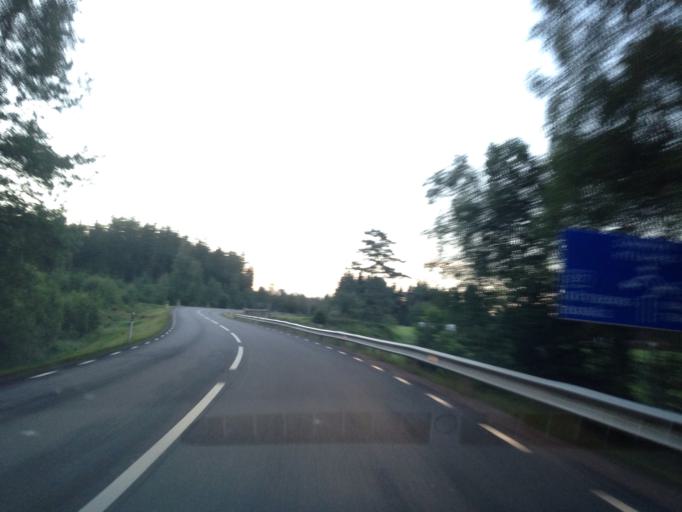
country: SE
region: Vaestra Goetaland
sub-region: Tranemo Kommun
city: Langhem
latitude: 57.6051
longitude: 13.1373
